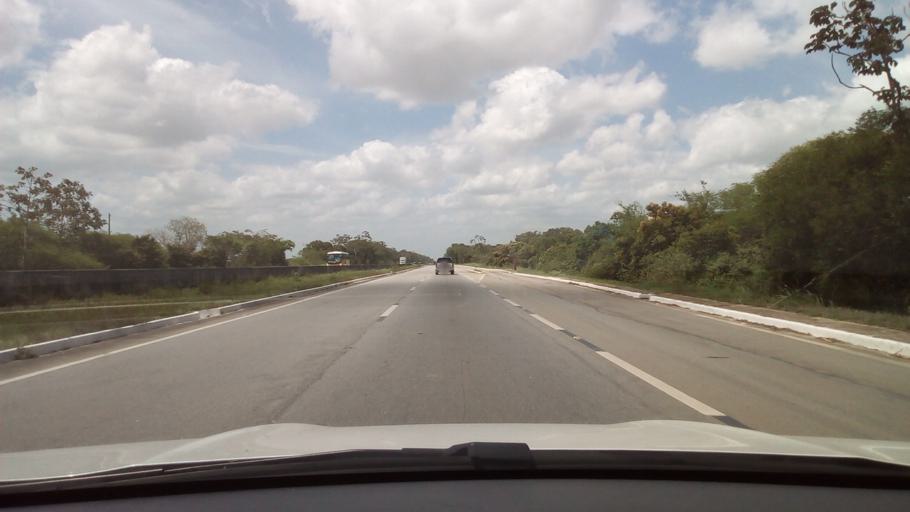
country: BR
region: Paraiba
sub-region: Mamanguape
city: Mamanguape
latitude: -6.9058
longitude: -35.1176
